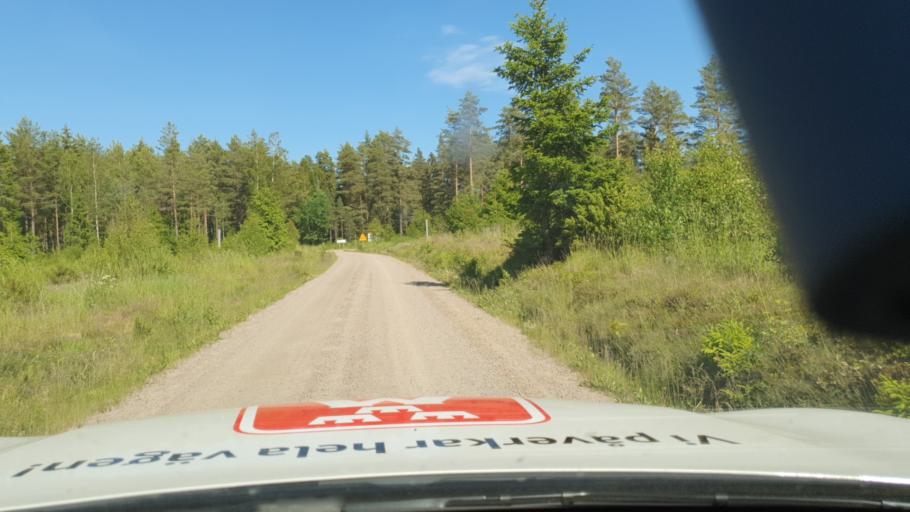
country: SE
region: Vaestra Goetaland
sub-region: Skovde Kommun
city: Skultorp
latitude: 58.3122
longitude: 13.8591
